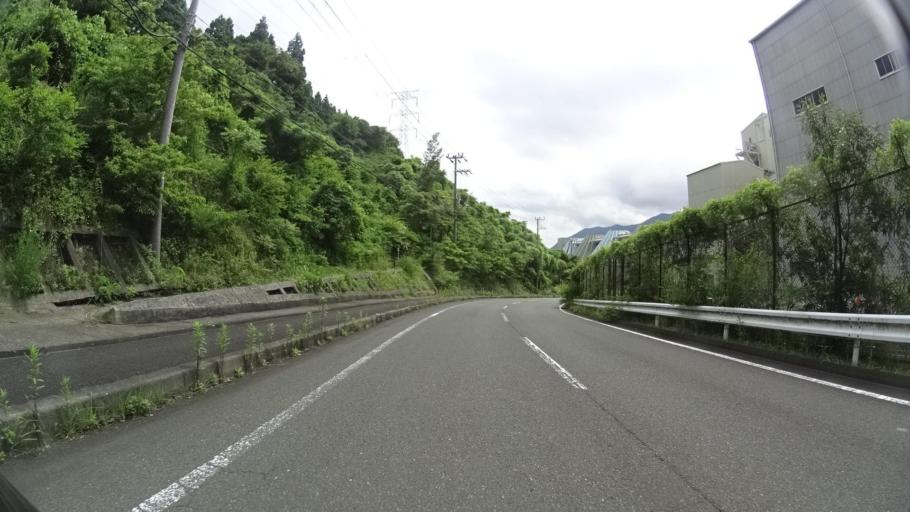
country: JP
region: Kyoto
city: Maizuru
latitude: 35.5296
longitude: 135.3461
